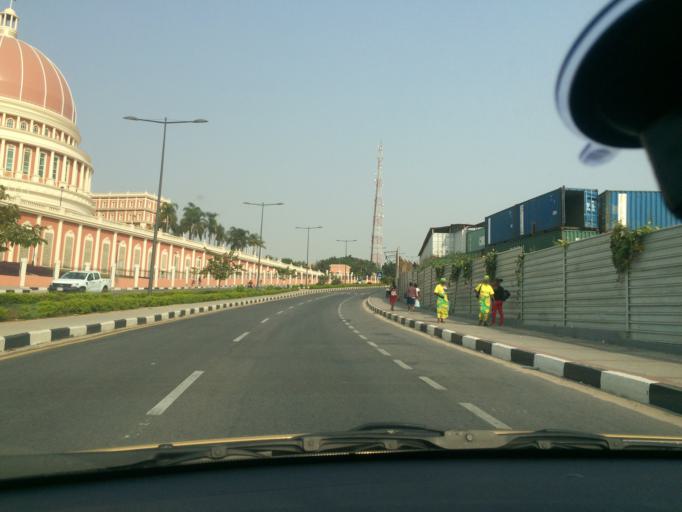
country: AO
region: Luanda
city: Luanda
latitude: -8.8220
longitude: 13.2227
